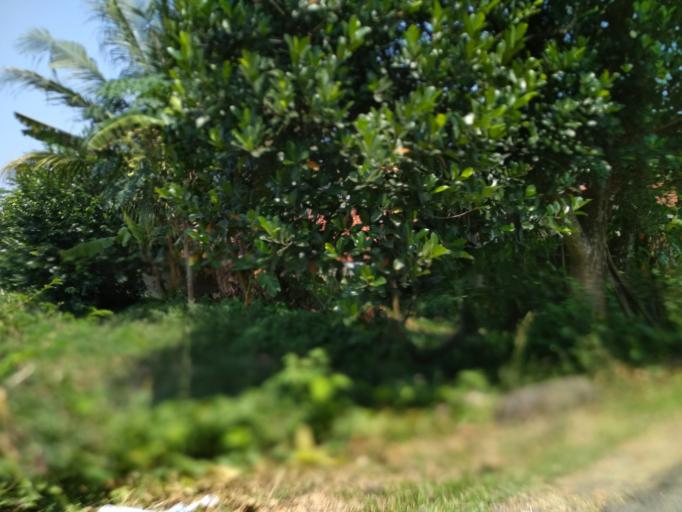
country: ID
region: West Java
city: Ciampea
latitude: -6.5515
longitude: 106.7379
